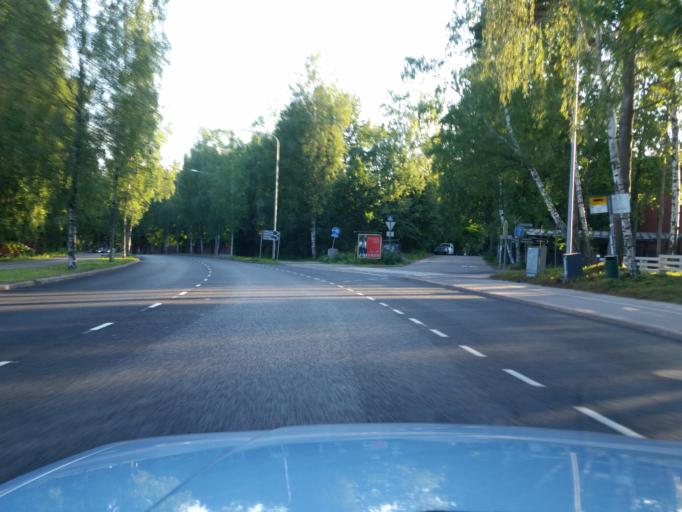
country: FI
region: Uusimaa
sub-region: Helsinki
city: Teekkarikylae
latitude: 60.1847
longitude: 24.8578
